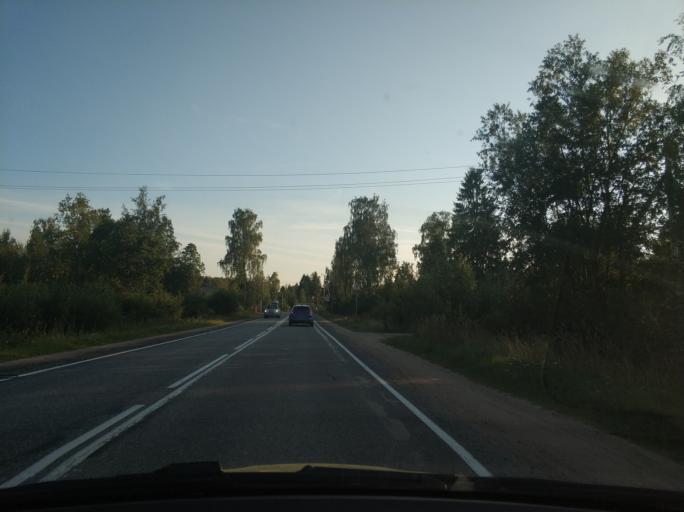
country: RU
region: Leningrad
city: Borisova Griva
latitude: 60.0924
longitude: 30.9603
